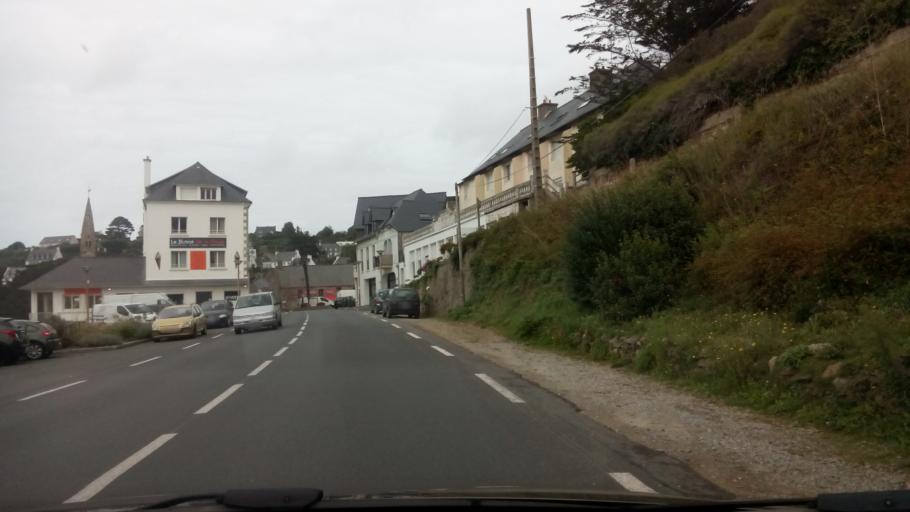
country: FR
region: Brittany
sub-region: Departement des Cotes-d'Armor
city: Locquemeau
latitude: 48.6835
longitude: -3.5671
